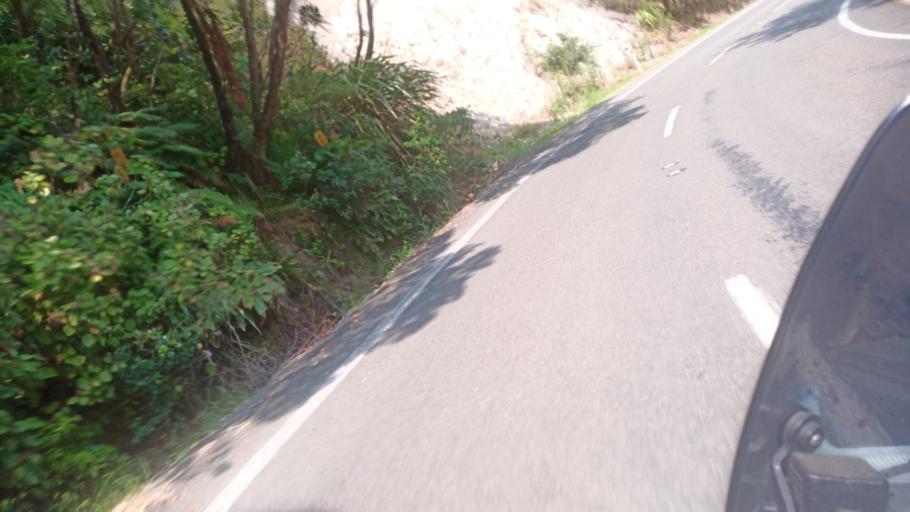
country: NZ
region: Bay of Plenty
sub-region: Opotiki District
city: Opotiki
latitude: -37.6095
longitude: 177.9613
